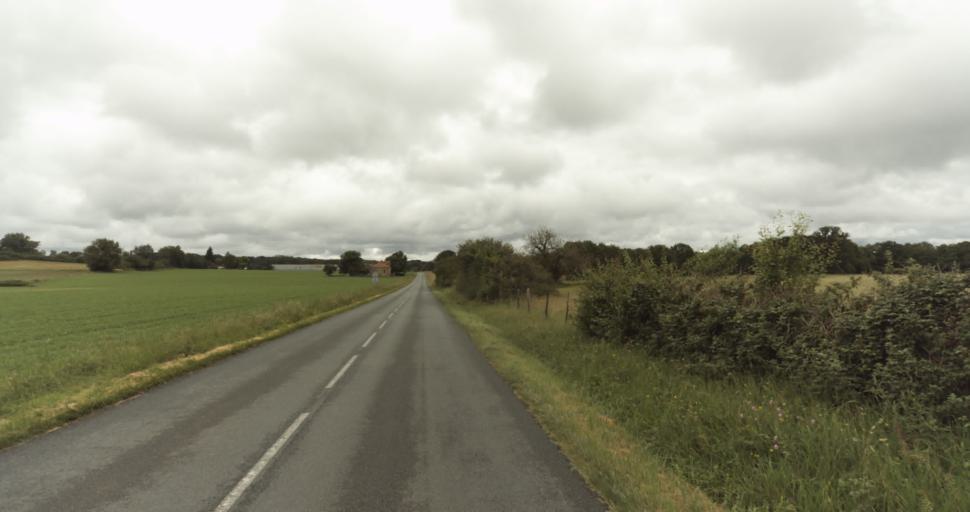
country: FR
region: Aquitaine
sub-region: Departement de la Dordogne
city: Belves
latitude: 44.6860
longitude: 0.9017
